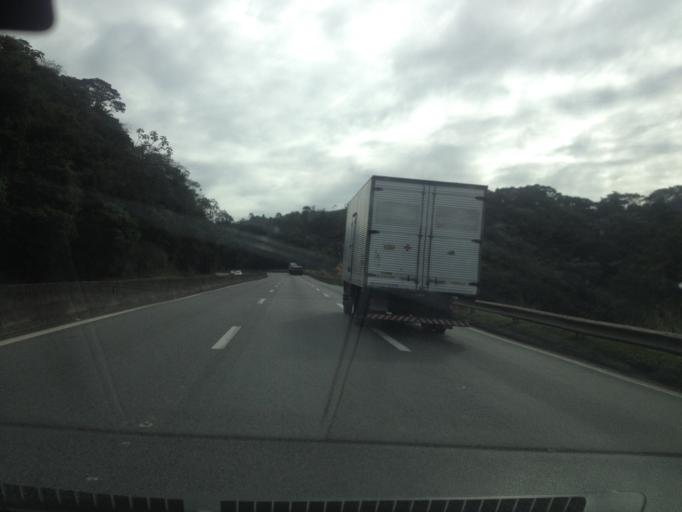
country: BR
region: Rio de Janeiro
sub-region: Pirai
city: Pirai
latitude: -22.6055
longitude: -43.9353
